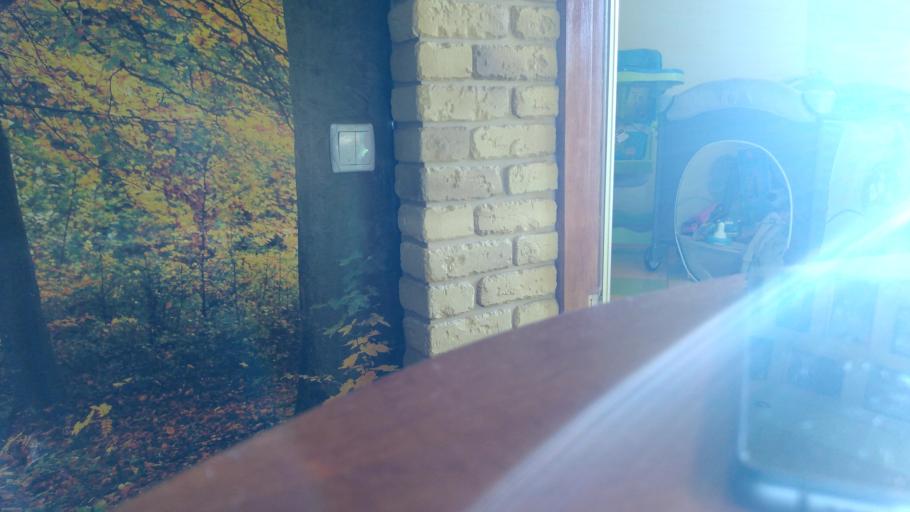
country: RU
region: Tverskaya
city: Likhoslavl'
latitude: 57.1299
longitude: 35.6450
